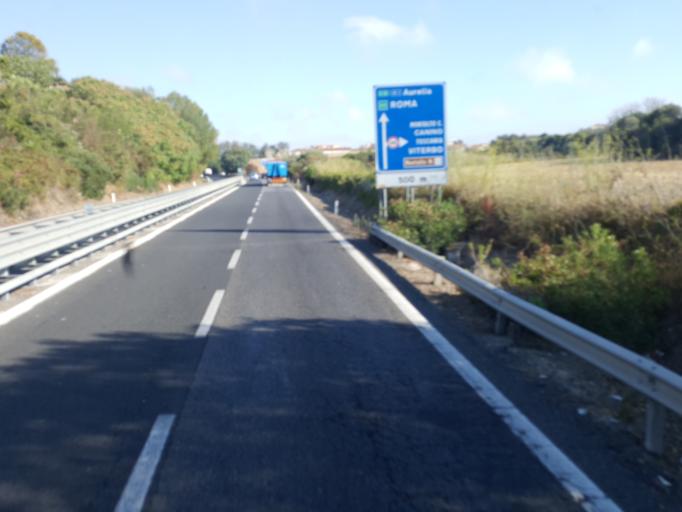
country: IT
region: Latium
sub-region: Provincia di Viterbo
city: Montalto di Castro
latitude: 42.3517
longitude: 11.5988
